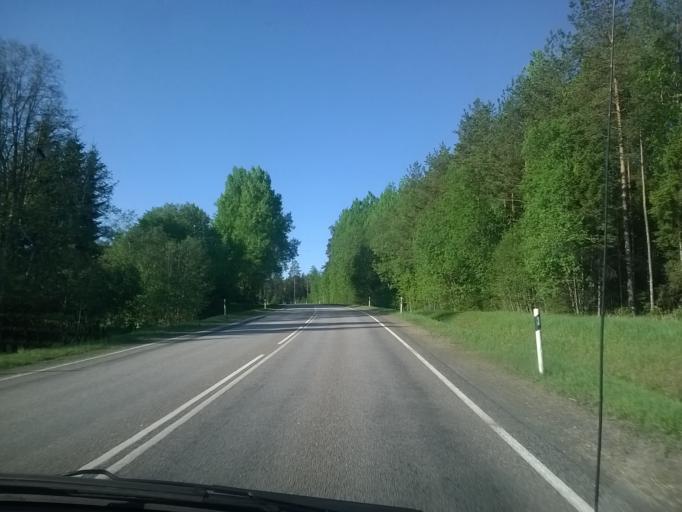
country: EE
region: Valgamaa
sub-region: Valga linn
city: Valga
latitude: 57.9762
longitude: 26.1687
